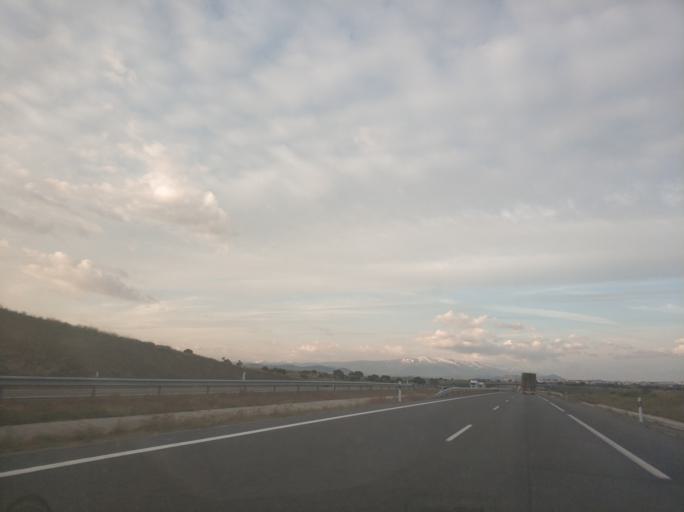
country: ES
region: Castille and Leon
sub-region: Provincia de Salamanca
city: Pizarral
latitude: 40.5909
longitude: -5.6543
